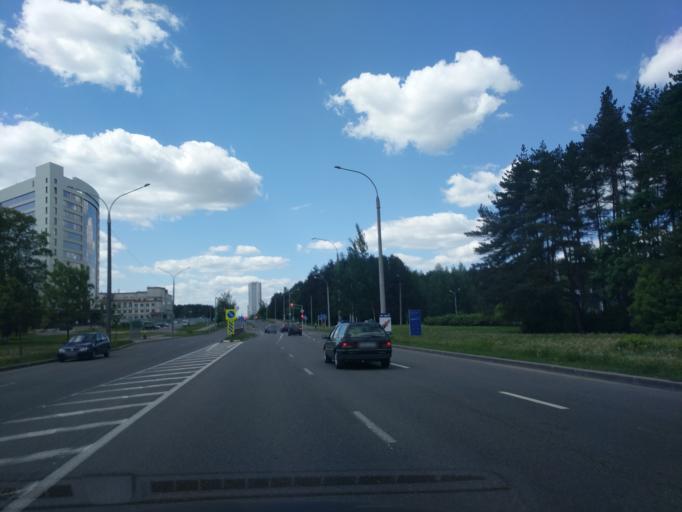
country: BY
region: Minsk
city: Borovlyany
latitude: 53.9244
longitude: 27.6685
